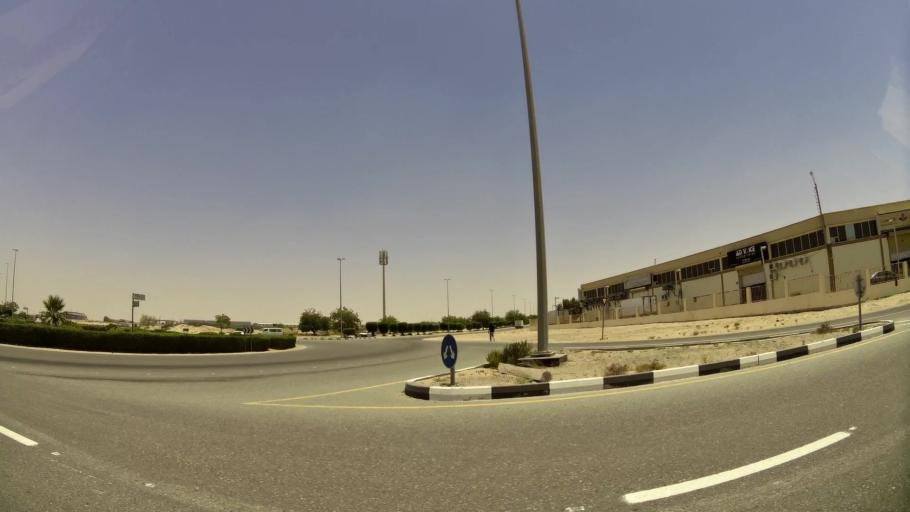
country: AE
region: Dubai
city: Dubai
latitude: 24.9795
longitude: 55.1767
